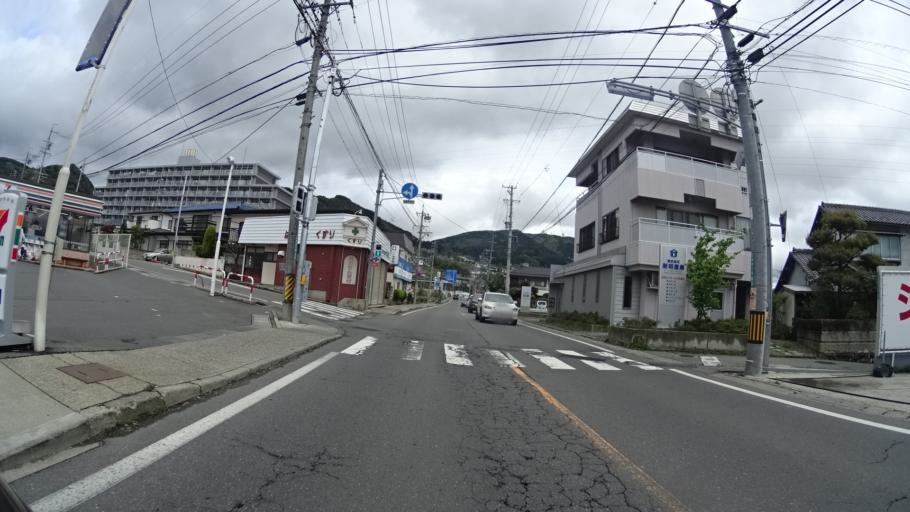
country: JP
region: Nagano
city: Nagano-shi
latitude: 36.6800
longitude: 138.2007
